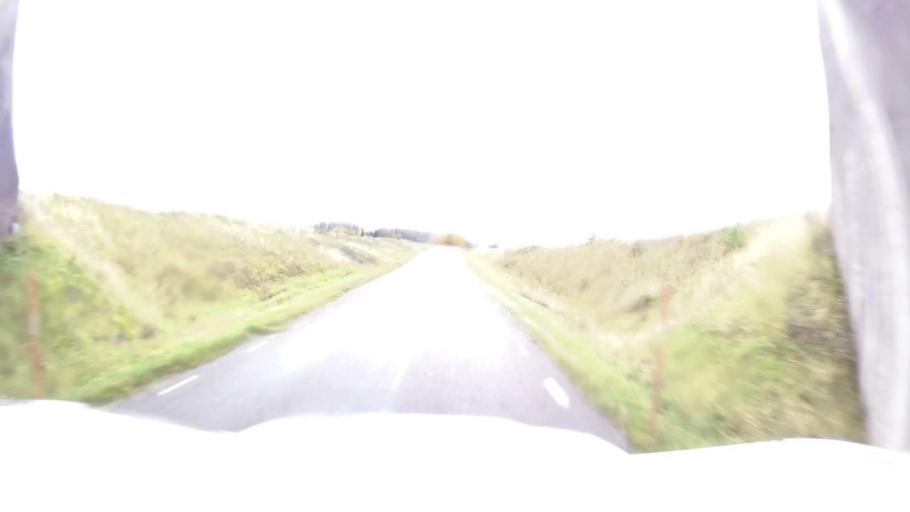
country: SE
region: OEstergoetland
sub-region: Linkopings Kommun
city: Linghem
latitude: 58.4721
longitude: 15.8205
